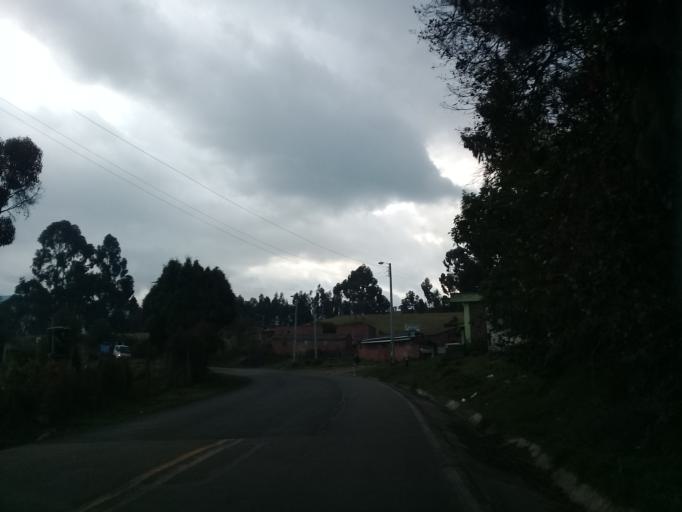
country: CO
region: Cundinamarca
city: Zipaquira
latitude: 5.0410
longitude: -74.0464
